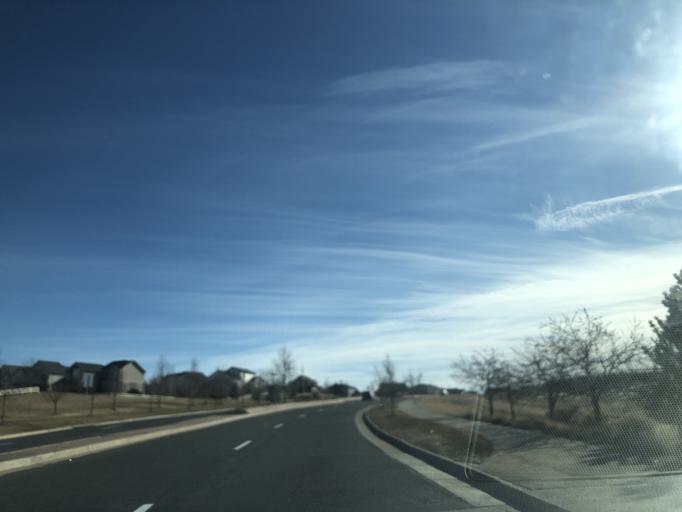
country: US
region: Colorado
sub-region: Arapahoe County
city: Dove Valley
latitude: 39.5606
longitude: -104.8085
